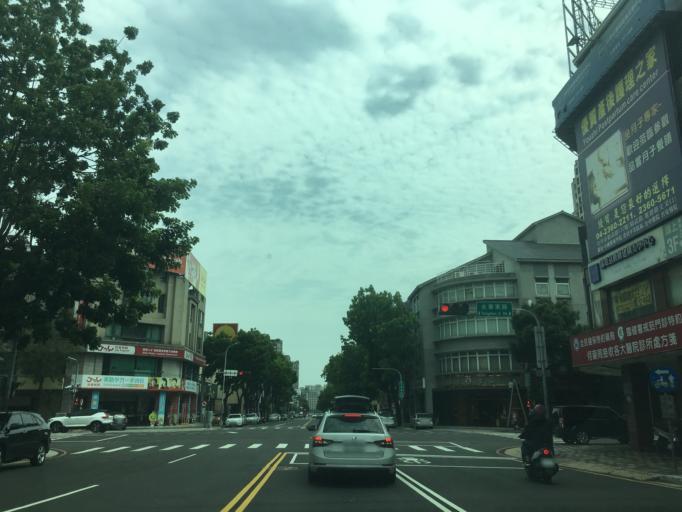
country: TW
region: Taiwan
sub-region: Taichung City
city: Taichung
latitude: 24.1353
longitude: 120.6499
